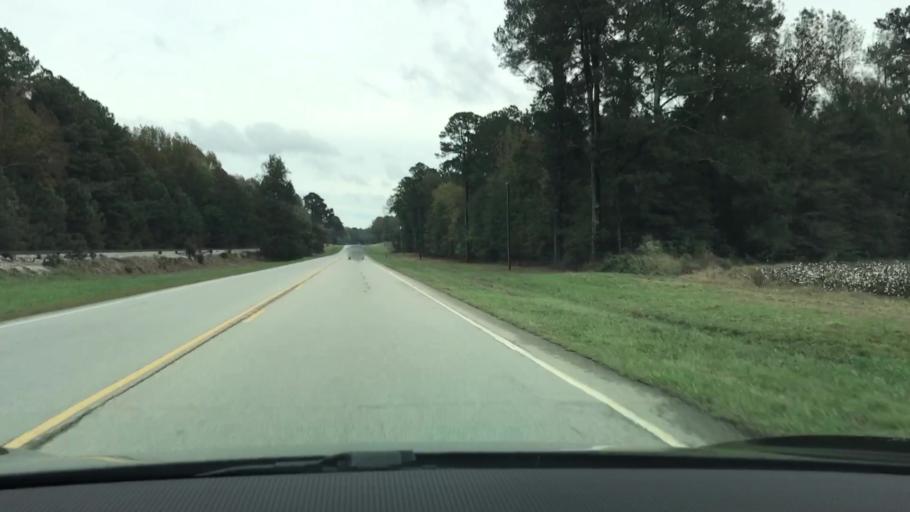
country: US
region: Georgia
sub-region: Warren County
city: Firing Range
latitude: 33.4731
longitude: -82.7249
